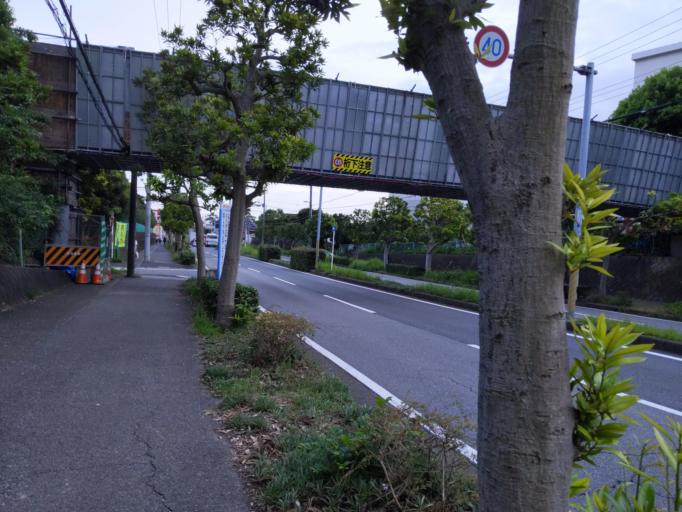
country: JP
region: Chiba
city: Funabashi
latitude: 35.7179
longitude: 139.9710
